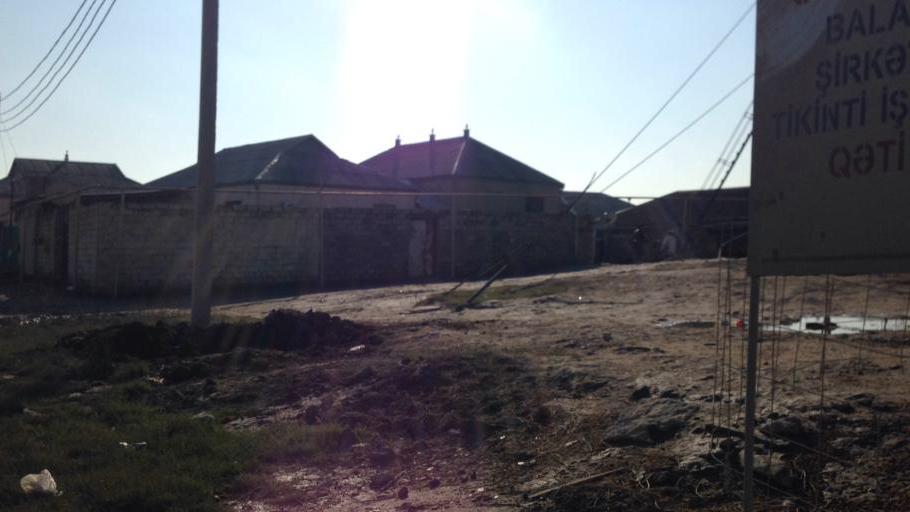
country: AZ
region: Baki
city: Sabuncu
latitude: 40.4493
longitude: 49.9315
